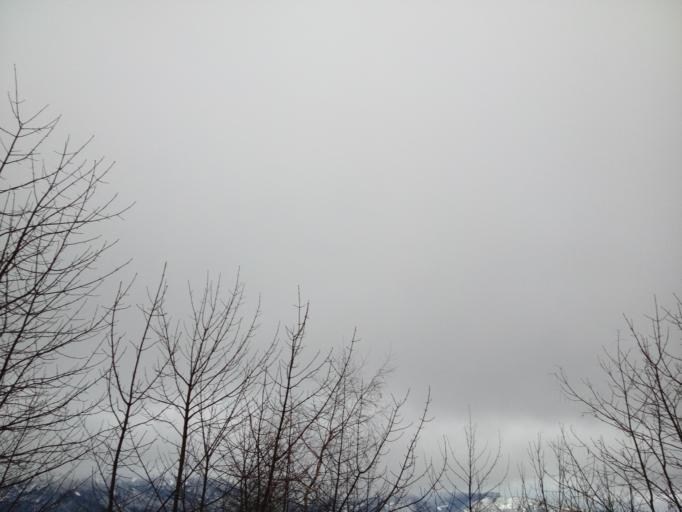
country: FR
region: Rhone-Alpes
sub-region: Departement de l'Isere
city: Noyarey
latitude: 45.2407
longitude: 5.5885
